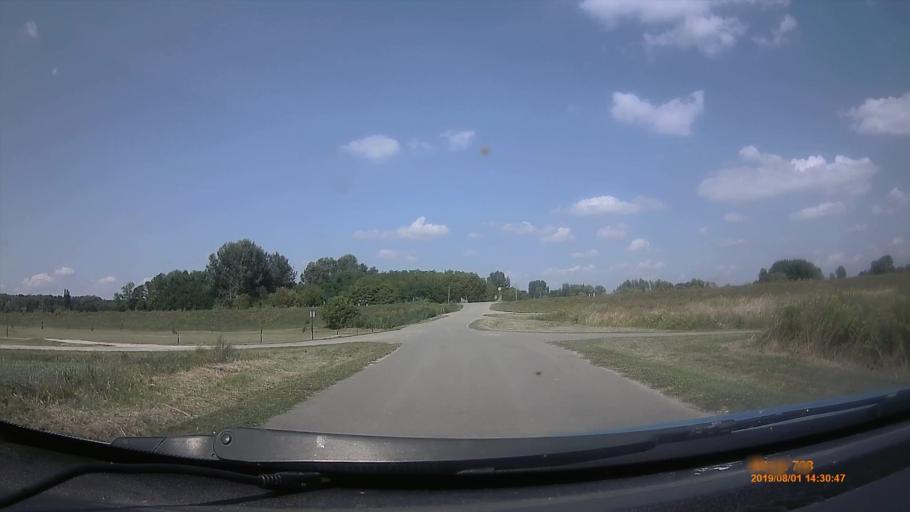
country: HR
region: Osjecko-Baranjska
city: Viljevo
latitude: 45.8058
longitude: 18.1018
